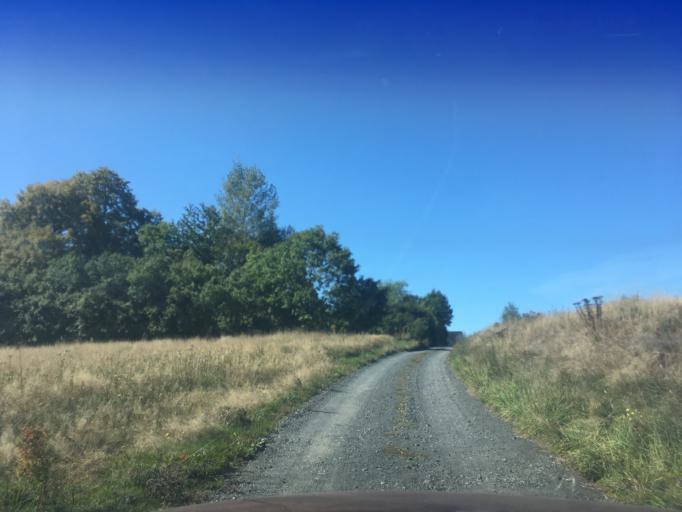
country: PL
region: Lower Silesian Voivodeship
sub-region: Powiat lubanski
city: Swieradow-Zdroj
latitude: 50.9634
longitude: 15.3190
